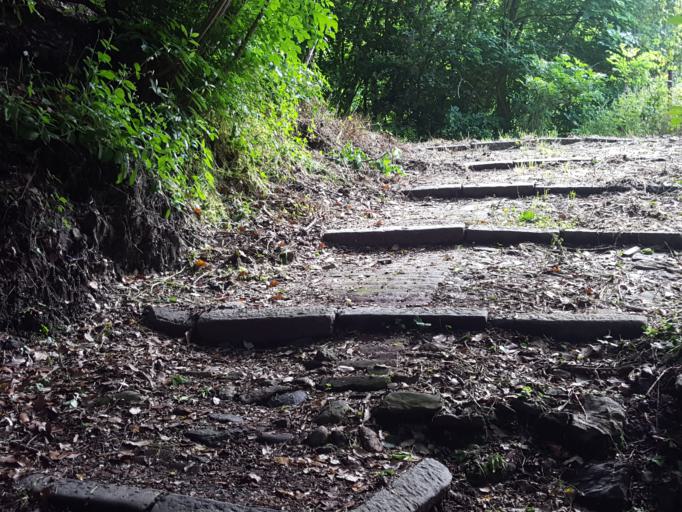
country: IT
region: Liguria
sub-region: Provincia di Genova
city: Manesseno
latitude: 44.4568
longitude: 8.9107
